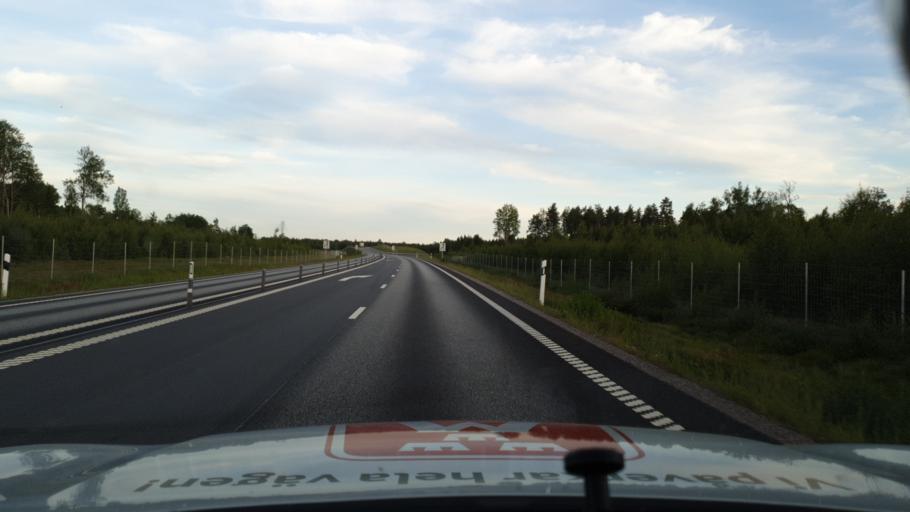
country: SE
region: OErebro
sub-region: Hallsbergs Kommun
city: Palsboda
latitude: 59.0701
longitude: 15.3111
